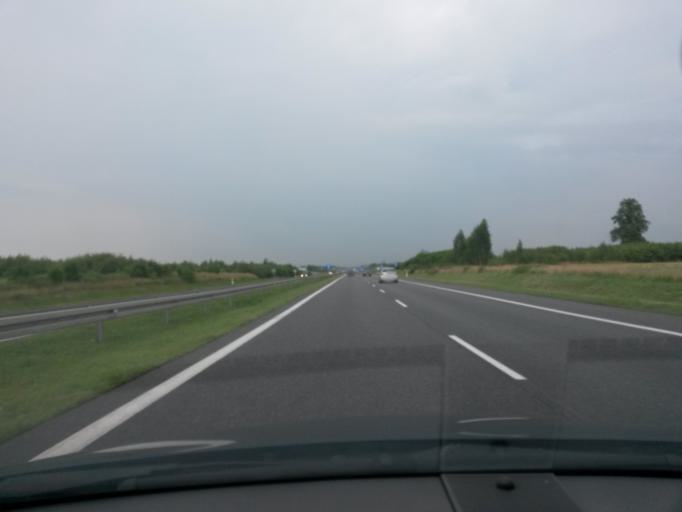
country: PL
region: Lodz Voivodeship
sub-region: Powiat piotrkowski
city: Wola Krzysztoporska
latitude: 51.3952
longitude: 19.6302
